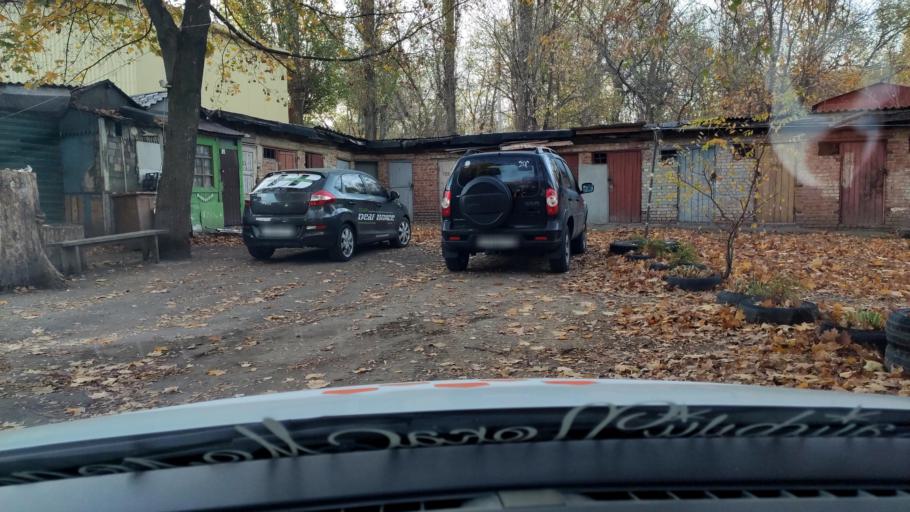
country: RU
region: Voronezj
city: Voronezh
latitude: 51.6917
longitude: 39.1677
